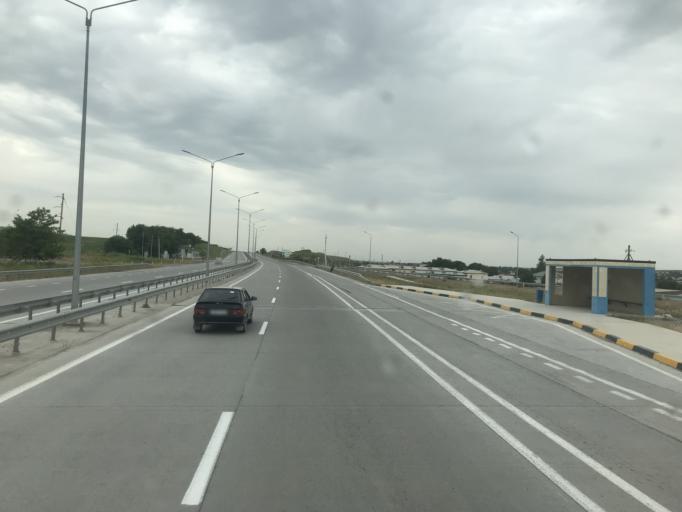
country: KZ
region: Ongtustik Qazaqstan
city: Qazyqurt
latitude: 41.7576
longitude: 69.4009
